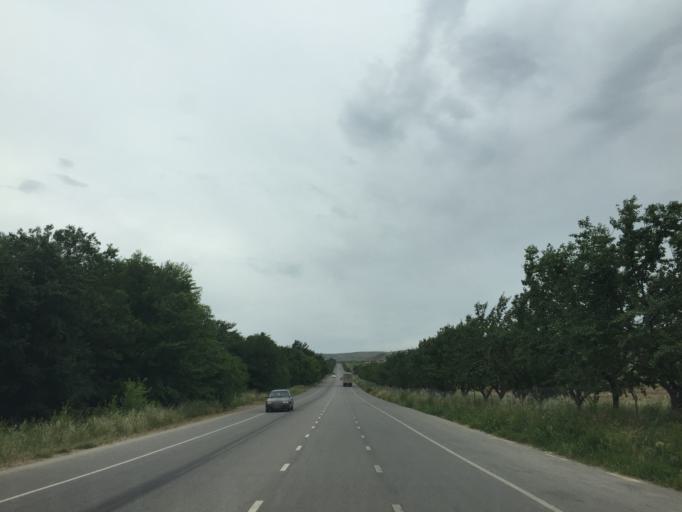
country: TJ
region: Republican Subordination
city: Vahdat
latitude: 38.5057
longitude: 69.1243
